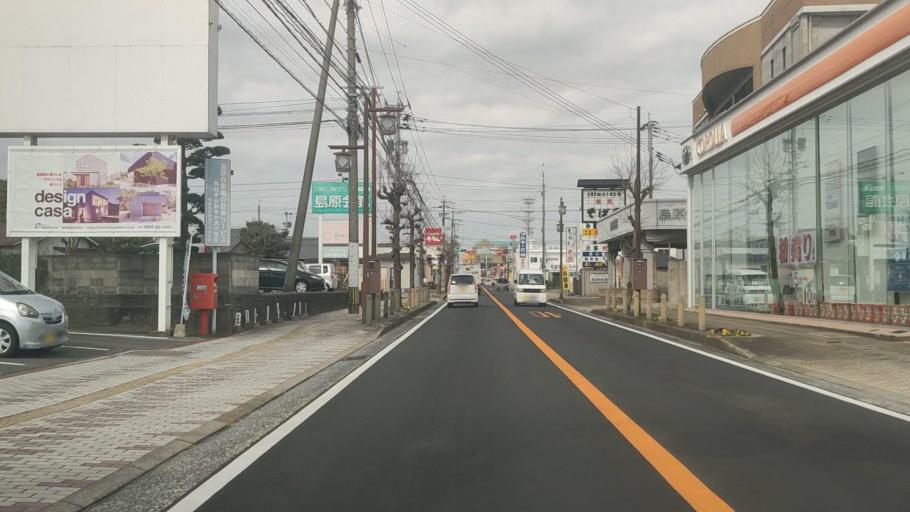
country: JP
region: Nagasaki
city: Shimabara
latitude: 32.7943
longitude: 130.3684
